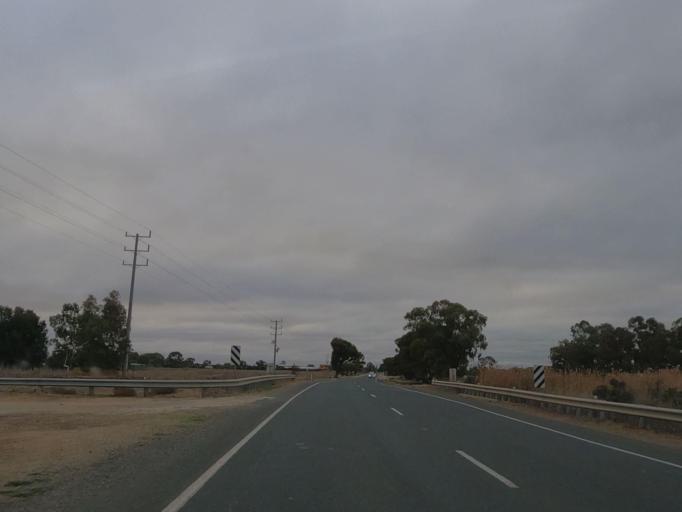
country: AU
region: Victoria
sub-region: Swan Hill
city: Swan Hill
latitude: -35.3952
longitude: 143.5727
